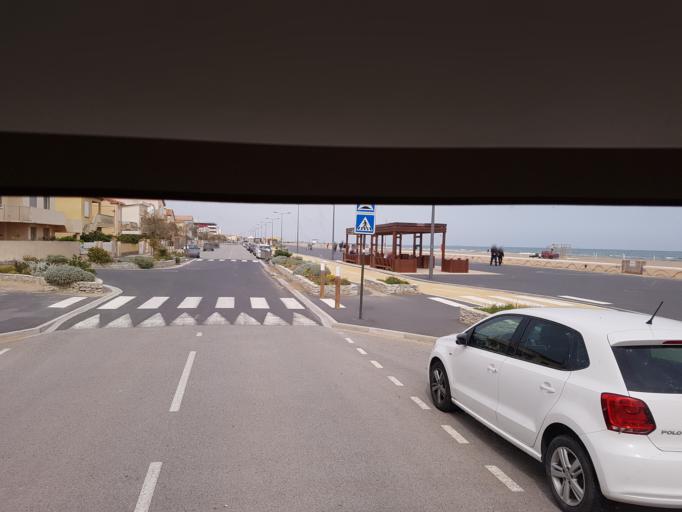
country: FR
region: Languedoc-Roussillon
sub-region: Departement de l'Aude
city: Armissan
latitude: 43.1554
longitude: 3.1642
